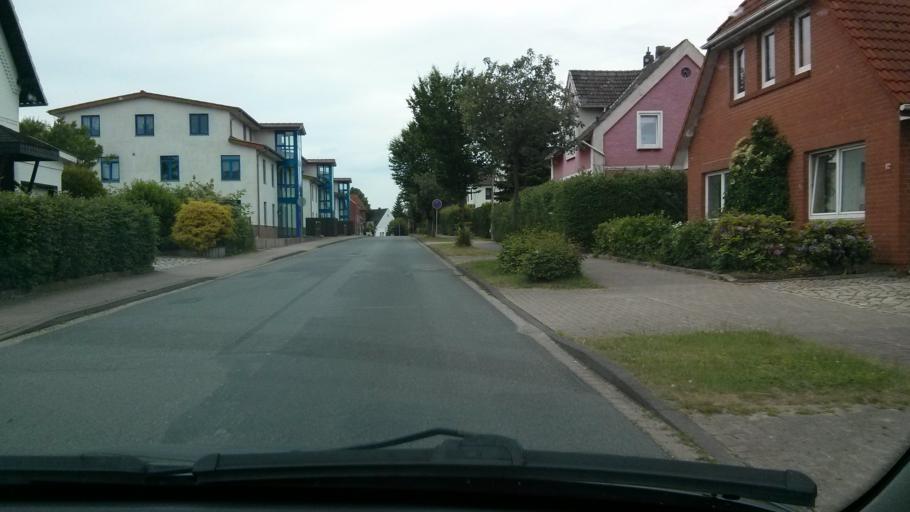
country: DE
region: Lower Saxony
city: Loxstedt
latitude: 53.4675
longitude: 8.6510
